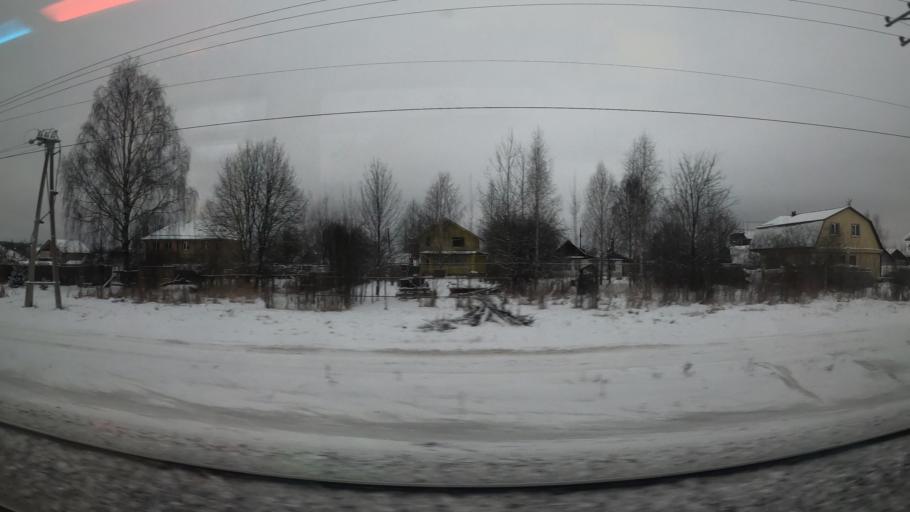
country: RU
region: Vladimir
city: Aleksandrov
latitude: 56.4080
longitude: 38.7415
